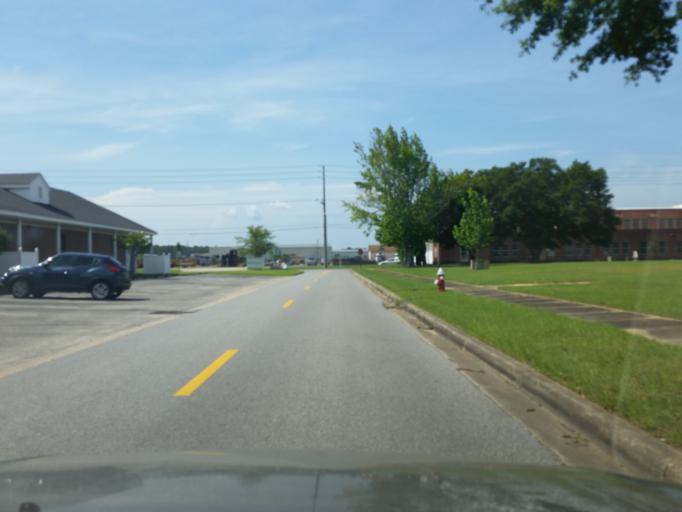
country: US
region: Florida
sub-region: Escambia County
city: Ferry Pass
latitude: 30.5288
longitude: -87.2004
